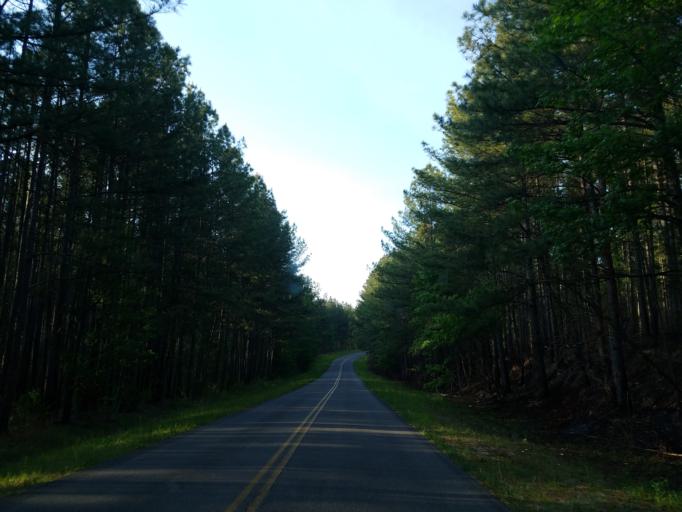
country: US
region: Georgia
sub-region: Gordon County
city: Calhoun
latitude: 34.5909
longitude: -85.0856
